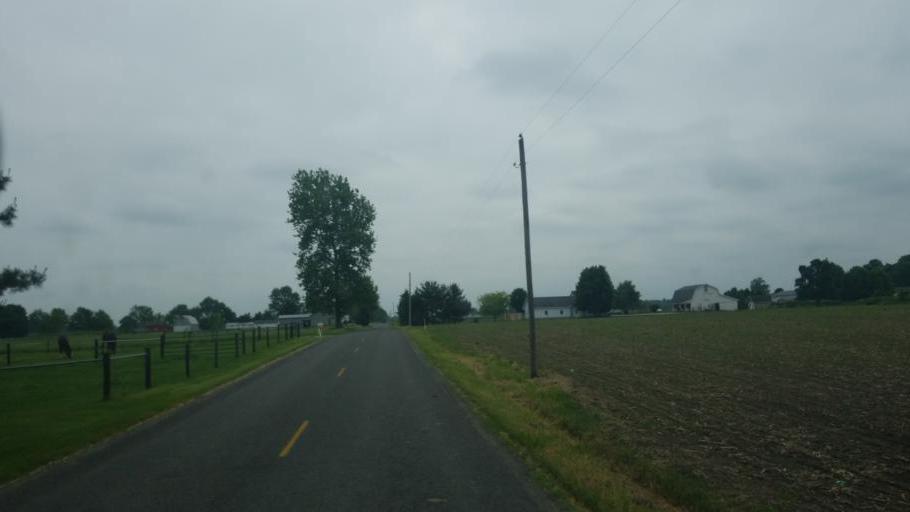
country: US
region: Indiana
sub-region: Elkhart County
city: Nappanee
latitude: 41.4697
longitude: -86.0498
